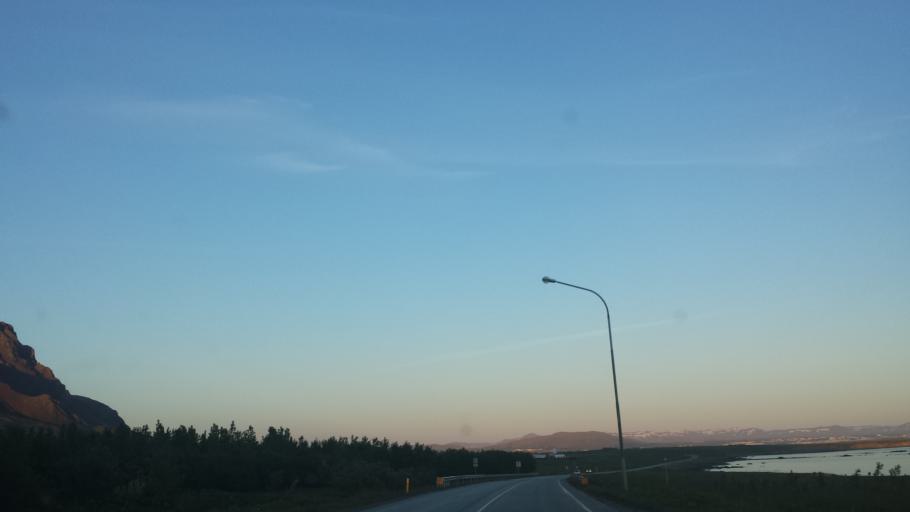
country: IS
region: Capital Region
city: Reykjavik
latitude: 64.2377
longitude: -21.8229
